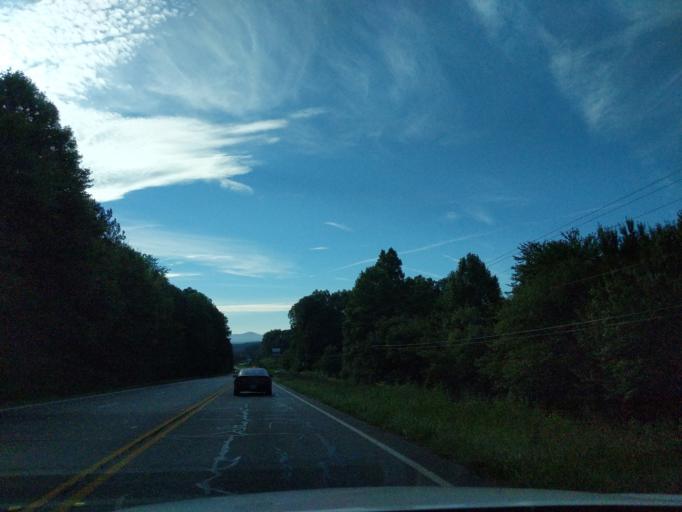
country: US
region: Georgia
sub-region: Fannin County
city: Blue Ridge
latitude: 34.9019
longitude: -84.3710
